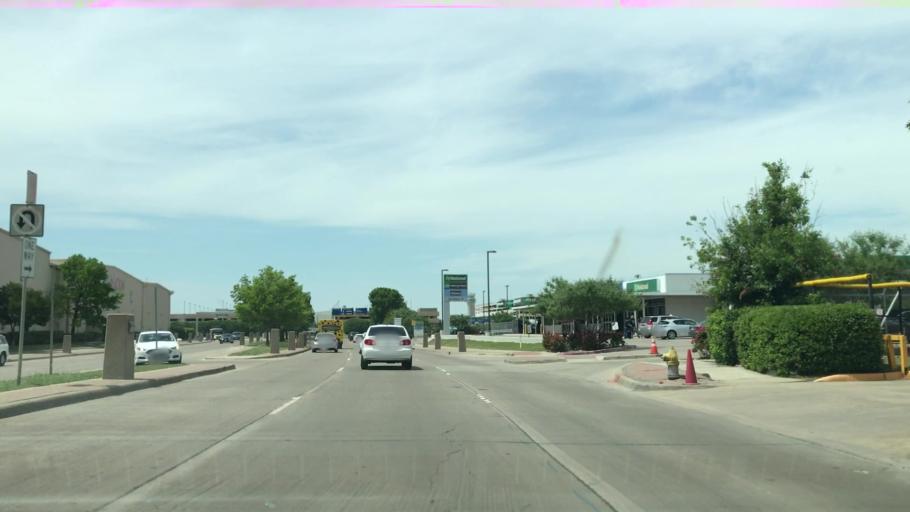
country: US
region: Texas
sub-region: Dallas County
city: University Park
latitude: 32.8379
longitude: -96.8436
